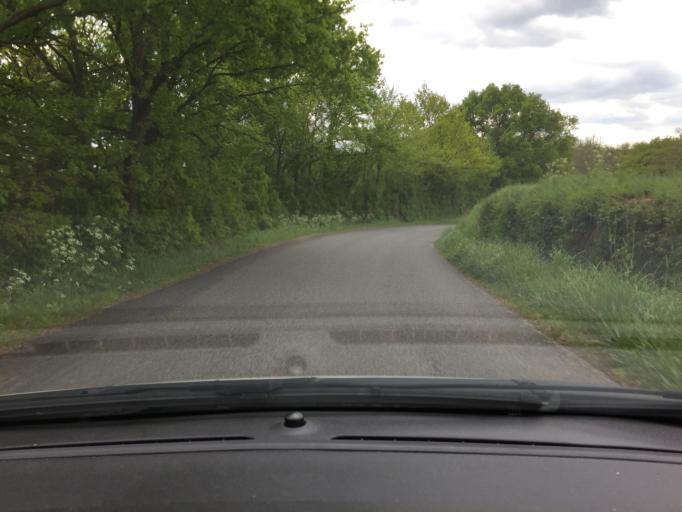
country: FR
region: Rhone-Alpes
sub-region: Departement du Rhone
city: Mornant
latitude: 45.6233
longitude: 4.6936
